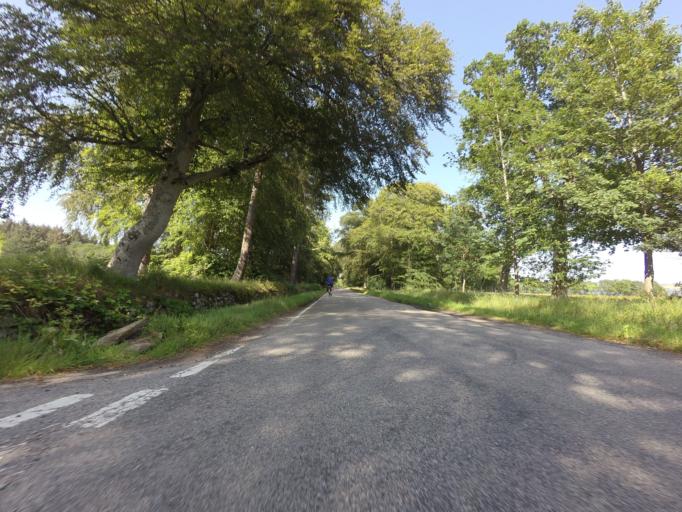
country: GB
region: Scotland
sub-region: Highland
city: Evanton
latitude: 57.6444
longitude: -4.3552
